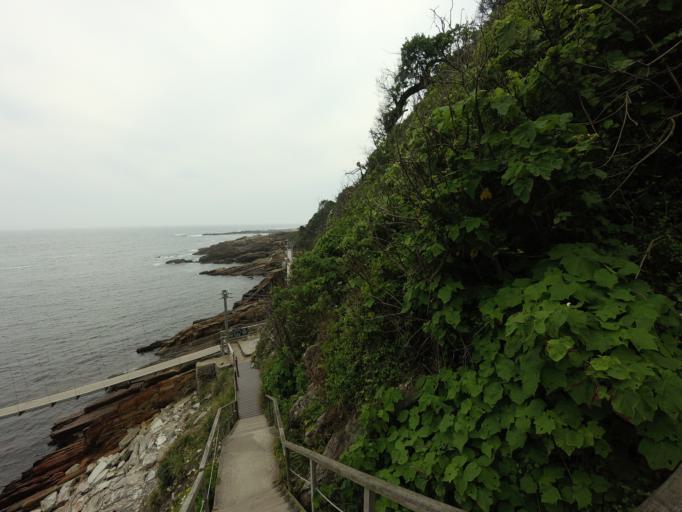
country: ZA
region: Eastern Cape
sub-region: Cacadu District Municipality
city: Kareedouw
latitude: -34.0192
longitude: 23.9033
